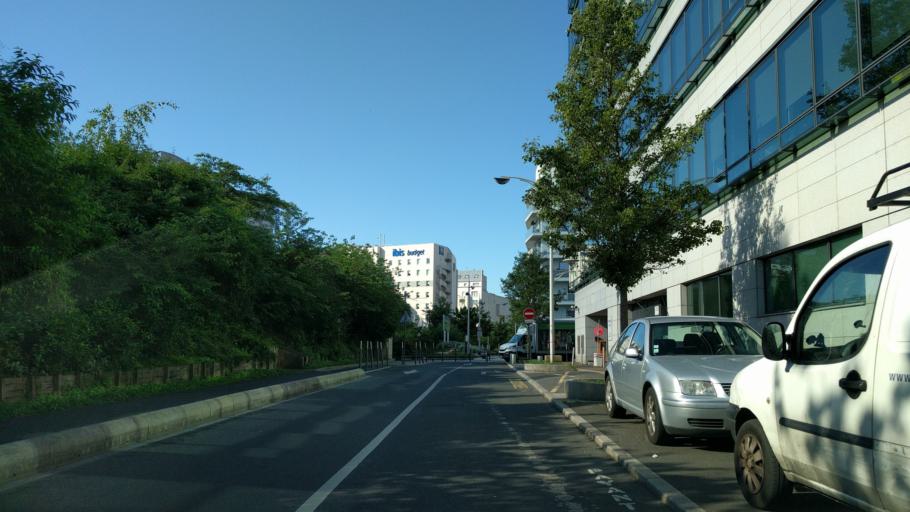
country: FR
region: Ile-de-France
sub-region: Departement des Hauts-de-Seine
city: Boulogne-Billancourt
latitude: 48.8259
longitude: 2.2611
